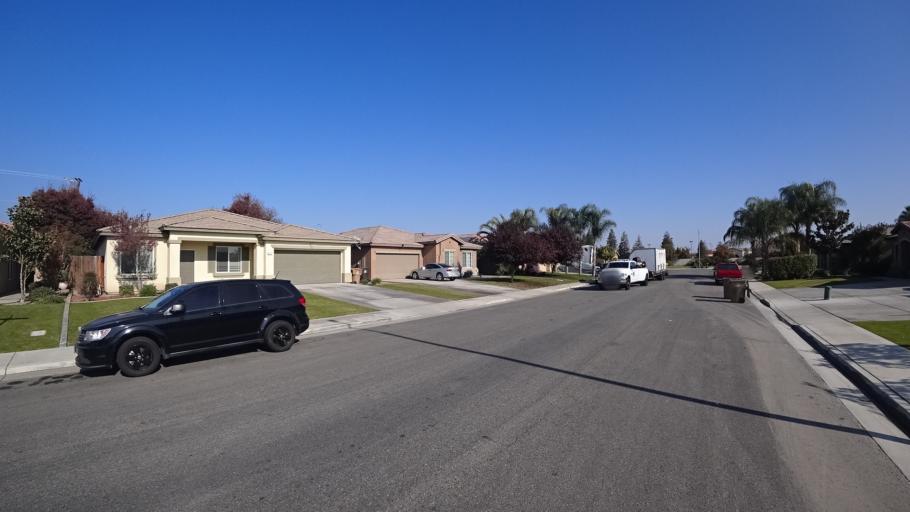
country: US
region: California
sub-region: Kern County
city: Greenfield
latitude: 35.2807
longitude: -119.0132
